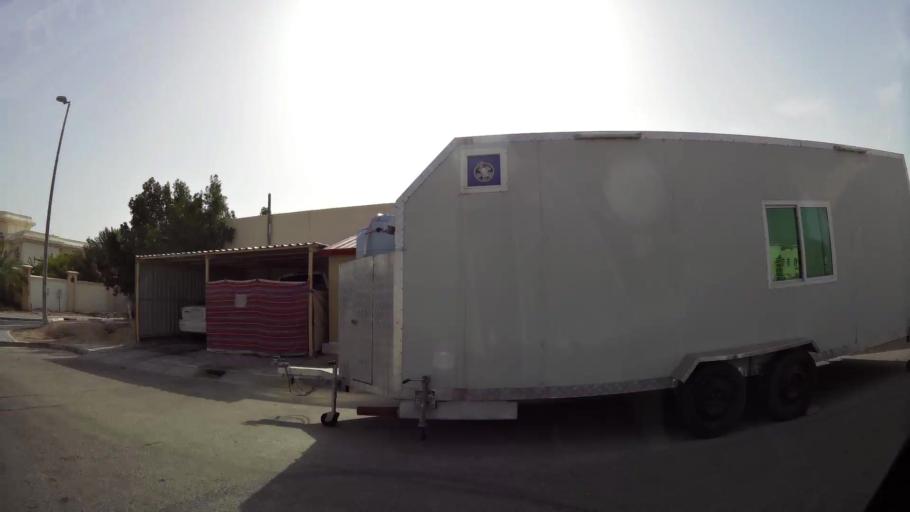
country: AE
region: Abu Dhabi
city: Al Ain
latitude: 24.1431
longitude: 55.7072
